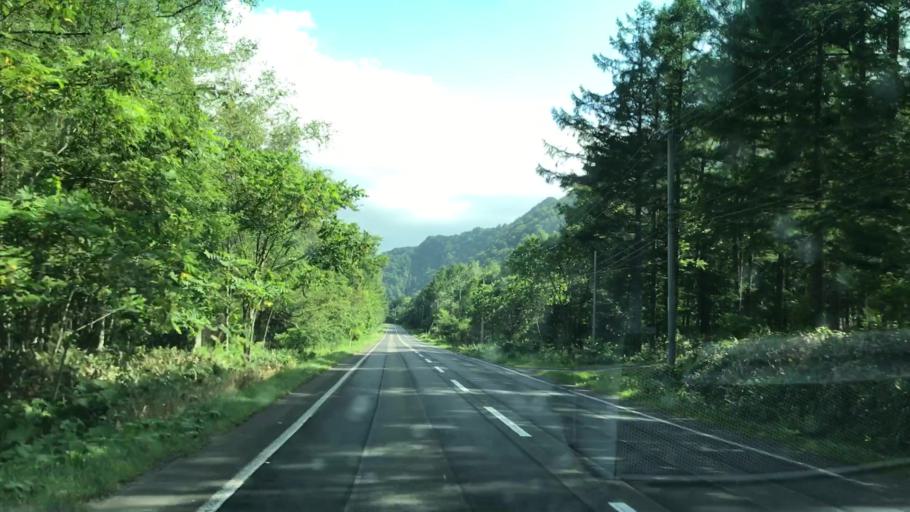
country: JP
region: Hokkaido
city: Shizunai-furukawacho
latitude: 42.8313
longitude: 142.4160
